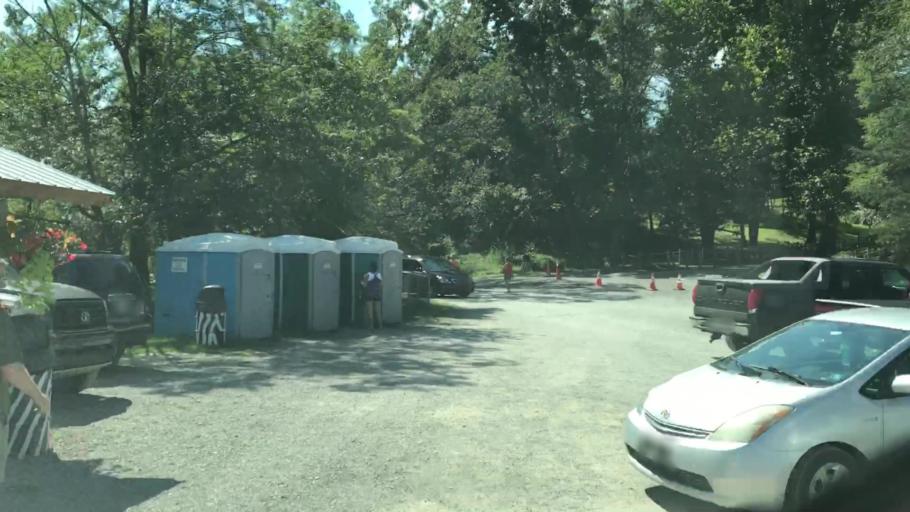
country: US
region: Pennsylvania
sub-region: Dauphin County
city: Matamoras
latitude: 40.5010
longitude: -76.8947
